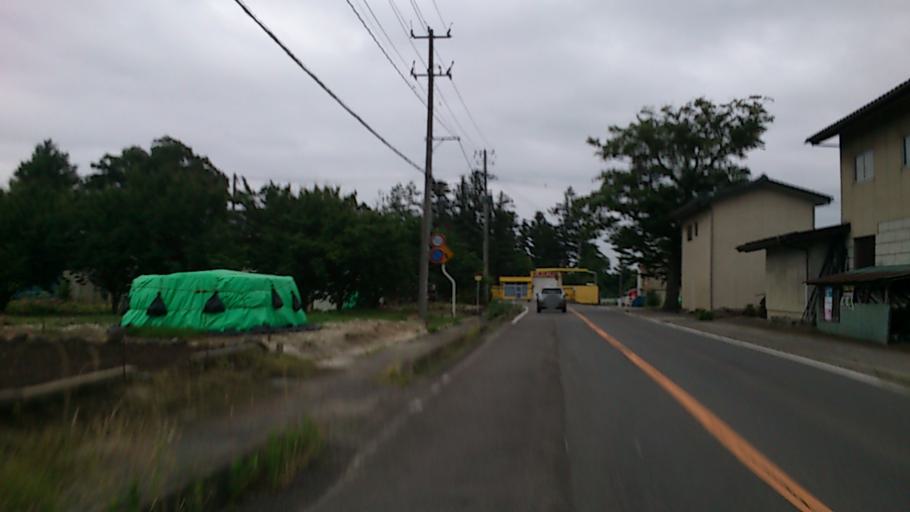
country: JP
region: Fukushima
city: Fukushima-shi
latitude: 37.7585
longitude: 140.3891
